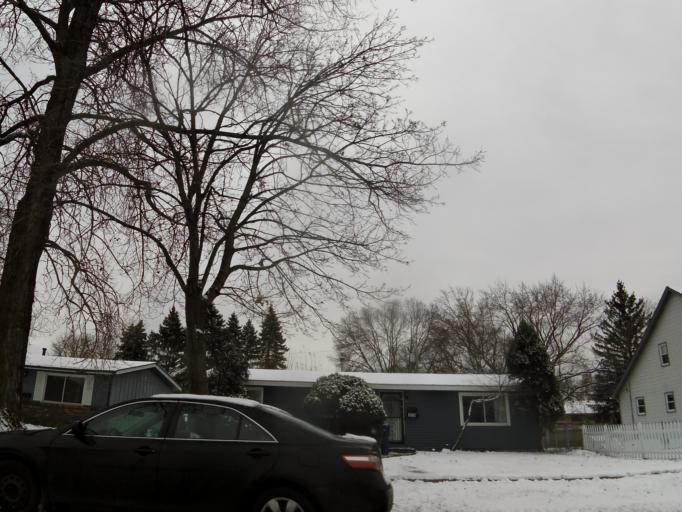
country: US
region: Minnesota
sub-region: Ramsey County
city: Maplewood
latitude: 44.9568
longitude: -93.0337
